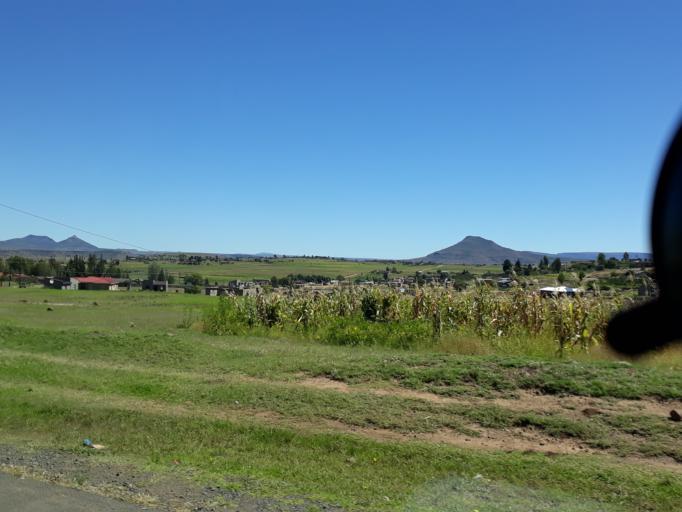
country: LS
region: Mohale's Hoek District
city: Mohale's Hoek
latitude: -30.1061
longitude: 27.4757
